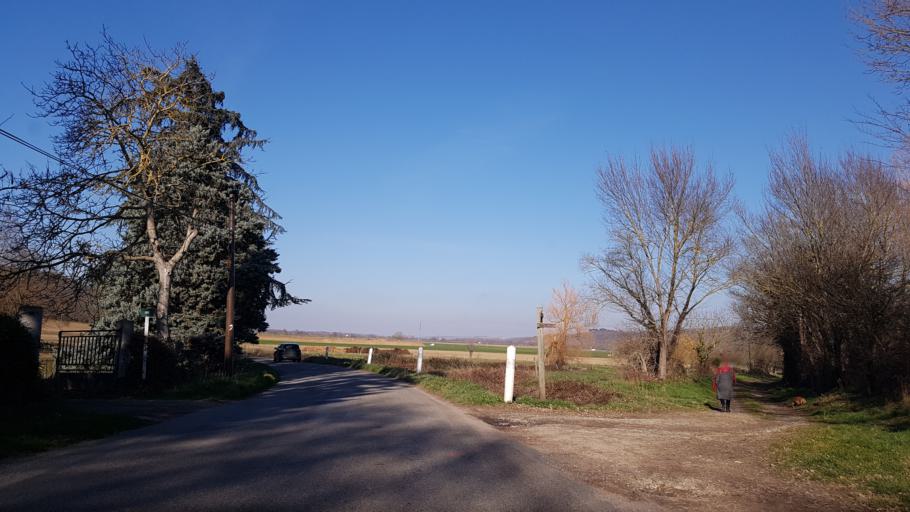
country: FR
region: Midi-Pyrenees
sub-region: Departement de l'Ariege
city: La Tour-du-Crieu
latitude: 43.1146
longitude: 1.7229
